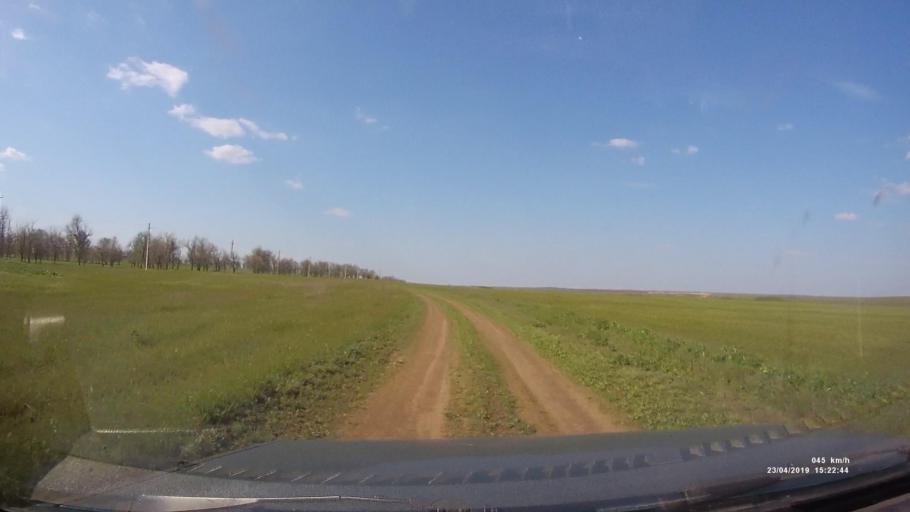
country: RU
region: Rostov
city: Remontnoye
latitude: 46.5310
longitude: 42.9705
